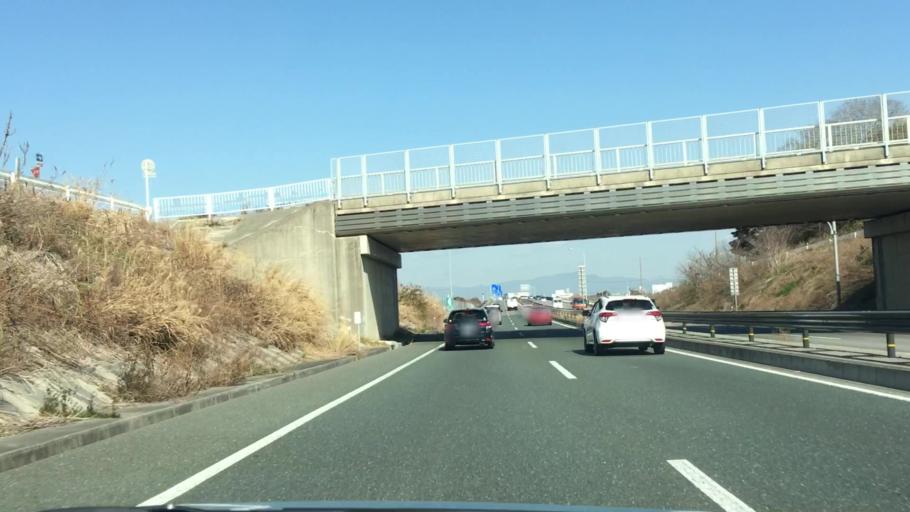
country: JP
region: Aichi
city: Toyohashi
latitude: 34.7160
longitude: 137.3525
